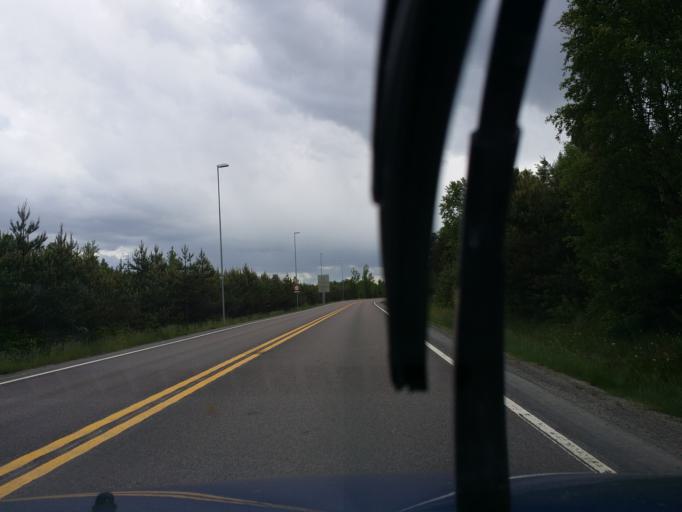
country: NO
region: Akershus
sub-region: Ullensaker
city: Jessheim
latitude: 60.1646
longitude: 11.1568
